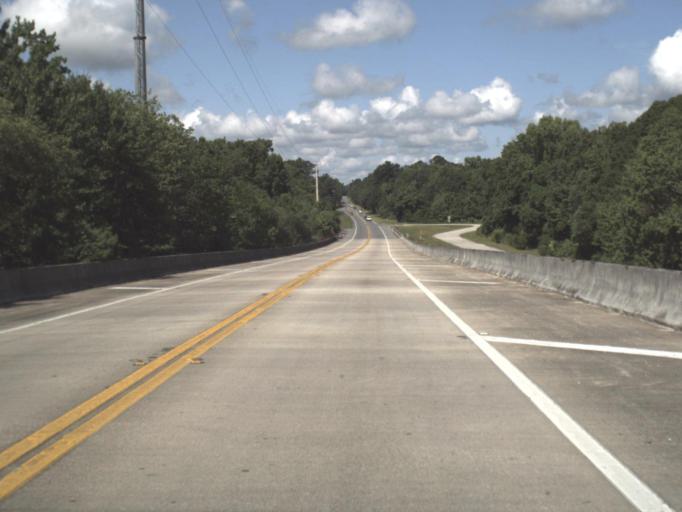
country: US
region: Florida
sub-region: Putnam County
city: Palatka
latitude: 29.5762
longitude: -81.6290
